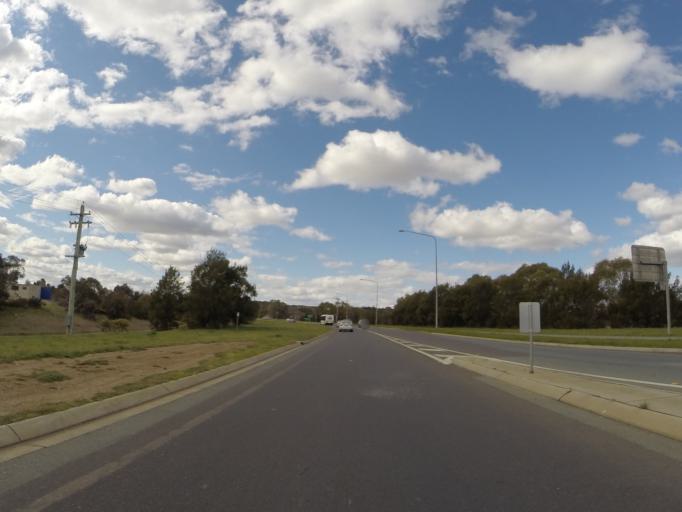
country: AU
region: Australian Capital Territory
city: Belconnen
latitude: -35.2156
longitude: 149.0852
